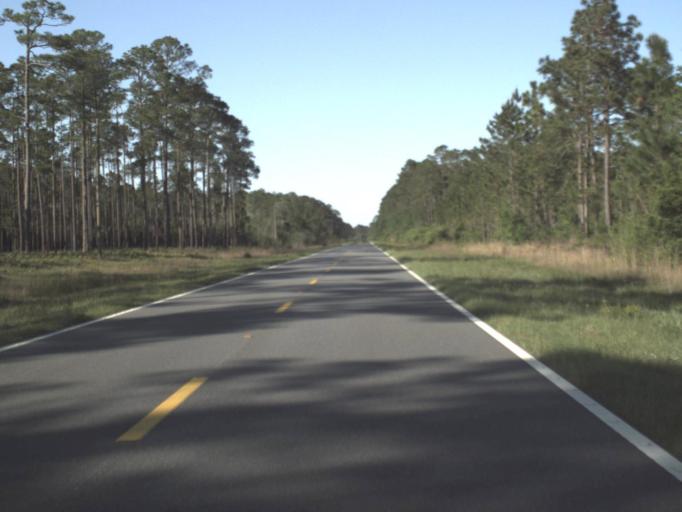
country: US
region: Florida
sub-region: Liberty County
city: Bristol
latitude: 30.2467
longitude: -84.8657
